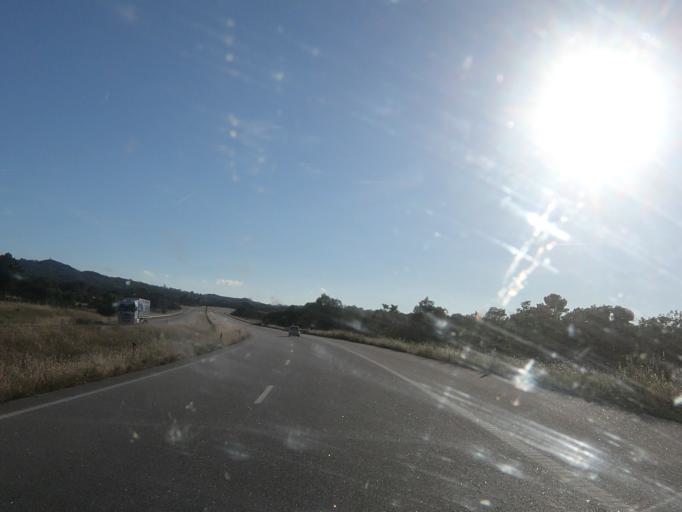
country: PT
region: Guarda
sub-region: Guarda
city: Sequeira
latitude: 40.6028
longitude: -7.1041
